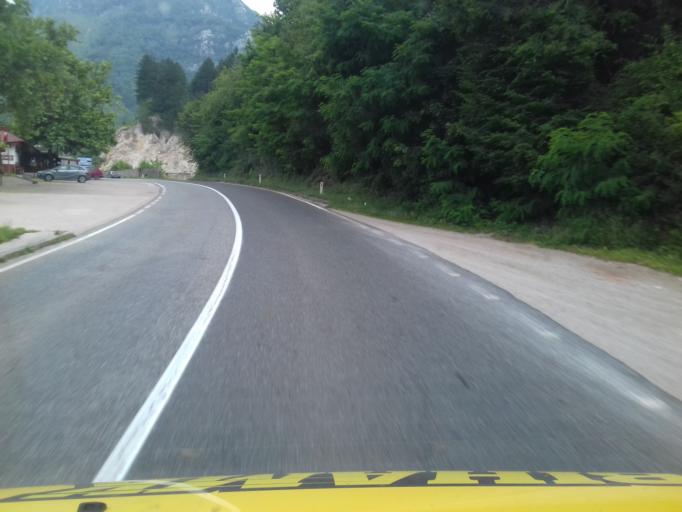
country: BA
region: Federation of Bosnia and Herzegovina
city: Jablanica
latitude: 43.6308
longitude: 17.7535
